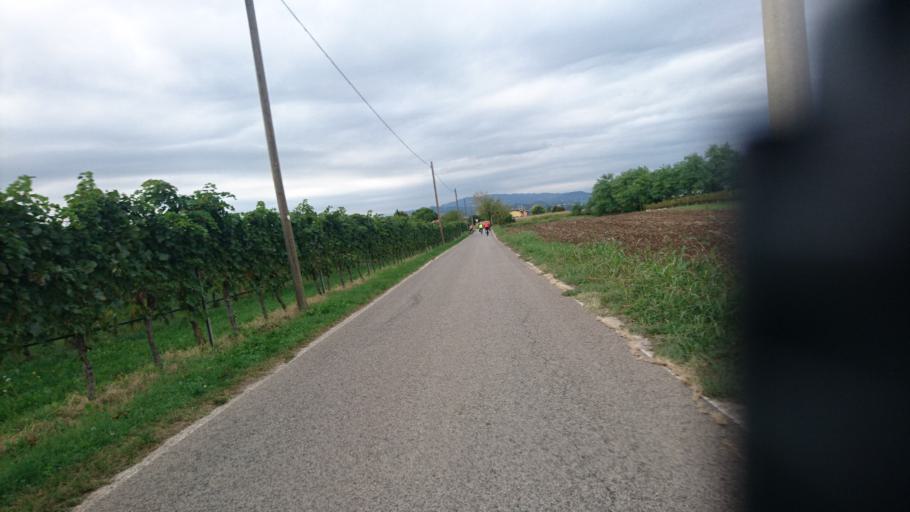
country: IT
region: Veneto
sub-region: Provincia di Vicenza
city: Montorso Vicentino
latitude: 45.4928
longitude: 11.3767
